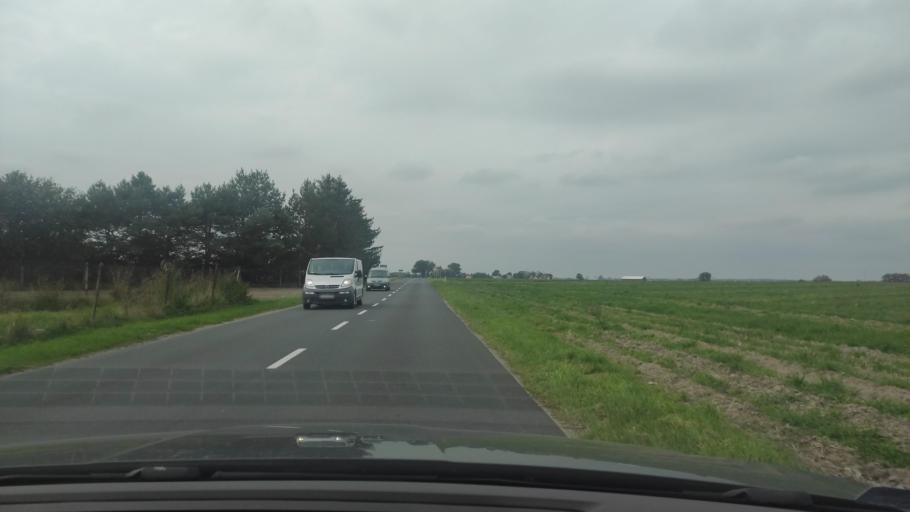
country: PL
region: Greater Poland Voivodeship
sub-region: Powiat poznanski
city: Swarzedz
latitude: 52.4228
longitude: 17.1517
